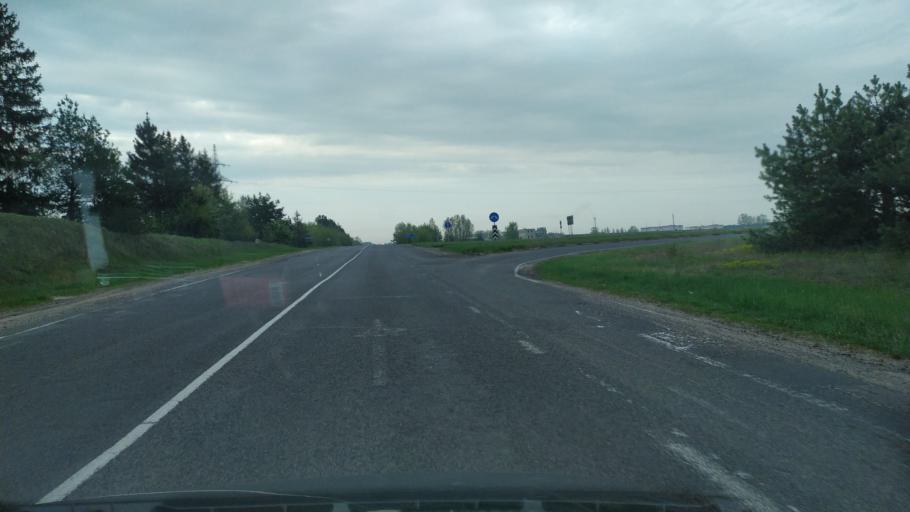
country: BY
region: Brest
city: Kamyanyets
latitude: 52.3407
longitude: 23.9075
